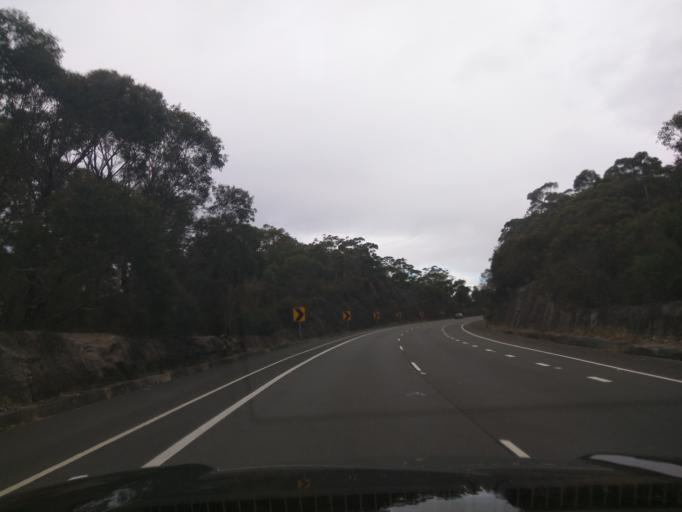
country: AU
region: New South Wales
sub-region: Wollongong
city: Helensburgh
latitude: -34.1427
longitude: 150.9943
